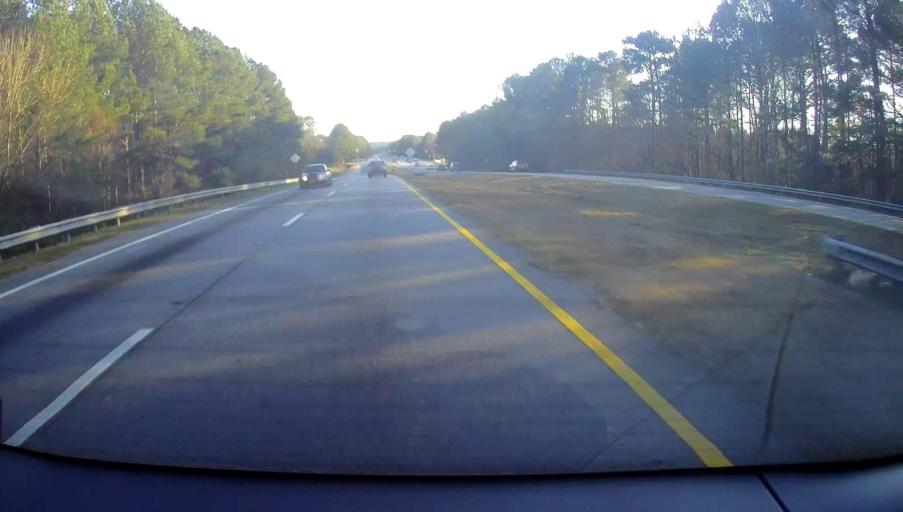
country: US
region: Georgia
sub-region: Fayette County
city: Tyrone
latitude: 33.4817
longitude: -84.5856
